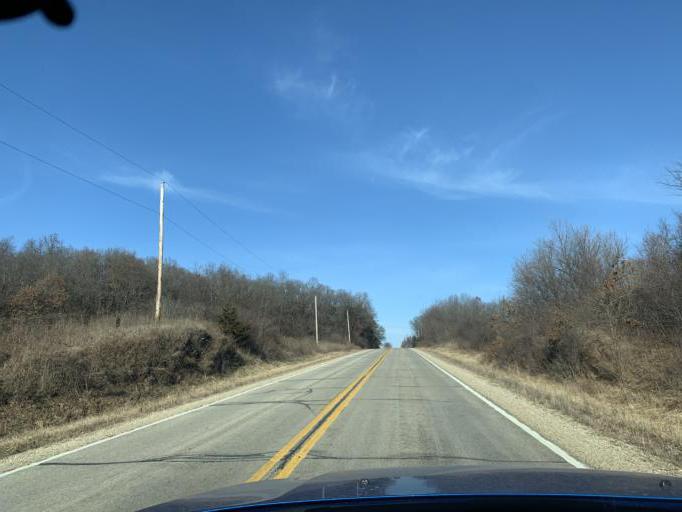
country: US
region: Wisconsin
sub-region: Green County
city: New Glarus
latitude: 42.7393
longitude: -89.8603
